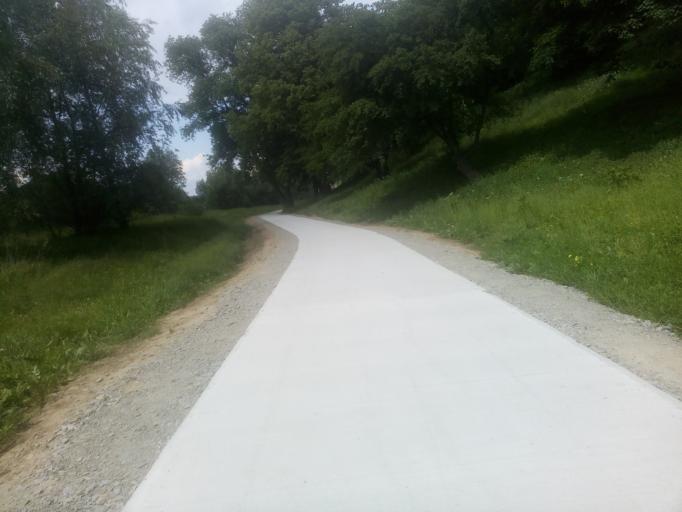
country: PL
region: Lesser Poland Voivodeship
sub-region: Powiat nowosadecki
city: Nowy Sacz
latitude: 49.6272
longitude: 20.6879
